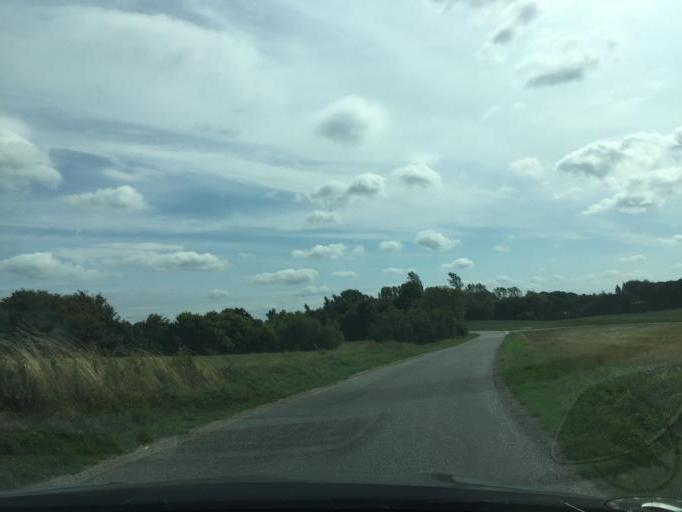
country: DK
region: South Denmark
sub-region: Assens Kommune
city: Tommerup Stationsby
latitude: 55.3960
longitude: 10.2441
